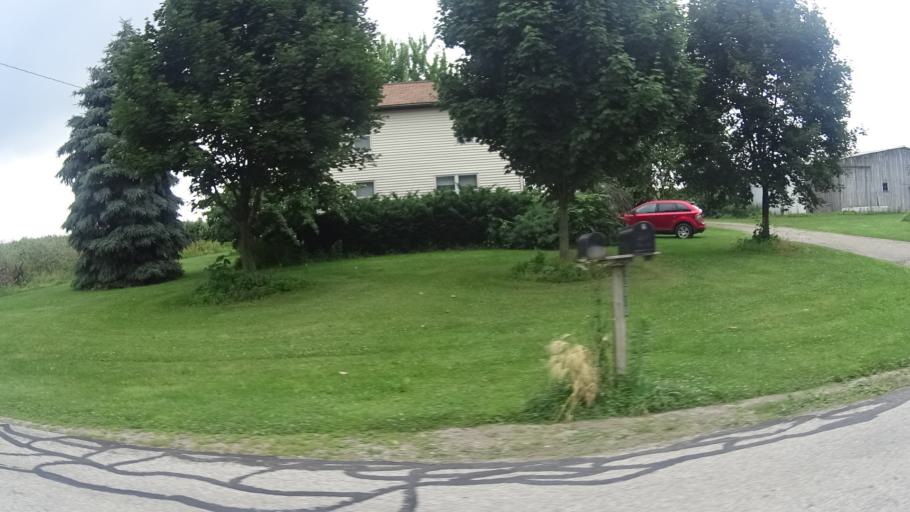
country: US
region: Ohio
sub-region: Huron County
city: Wakeman
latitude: 41.3148
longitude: -82.4815
